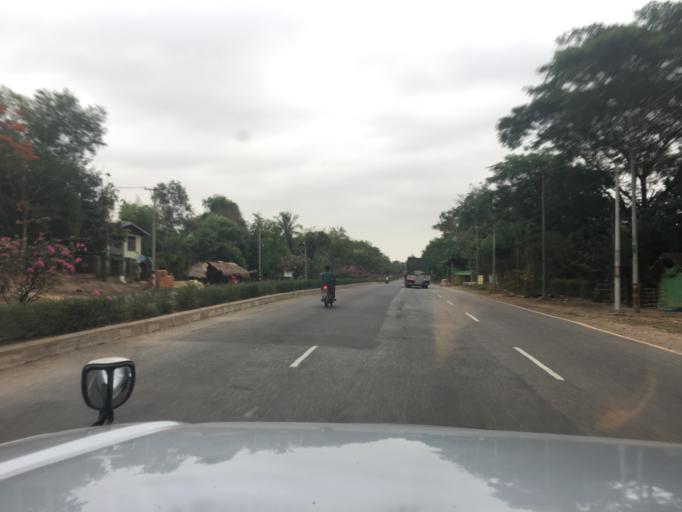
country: MM
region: Bago
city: Bago
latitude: 17.2214
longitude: 96.4387
